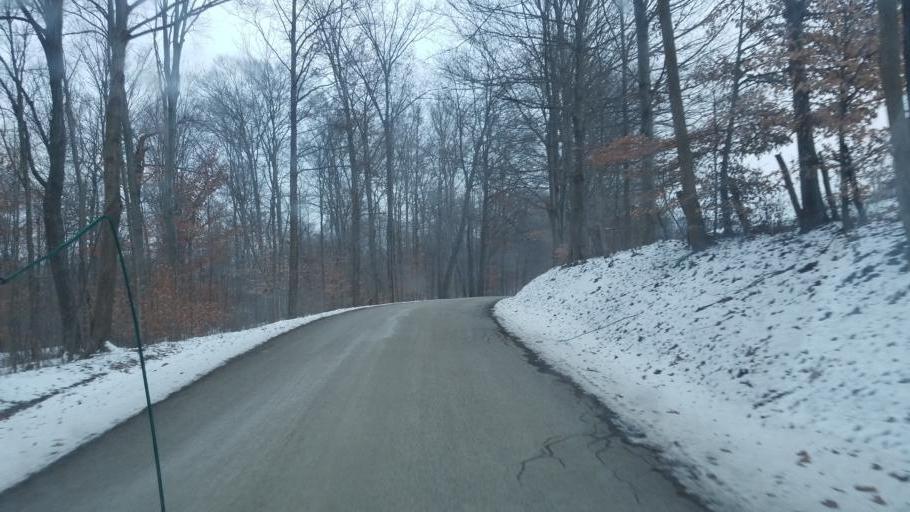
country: US
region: Ohio
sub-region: Richland County
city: Lincoln Heights
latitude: 40.6790
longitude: -82.3983
